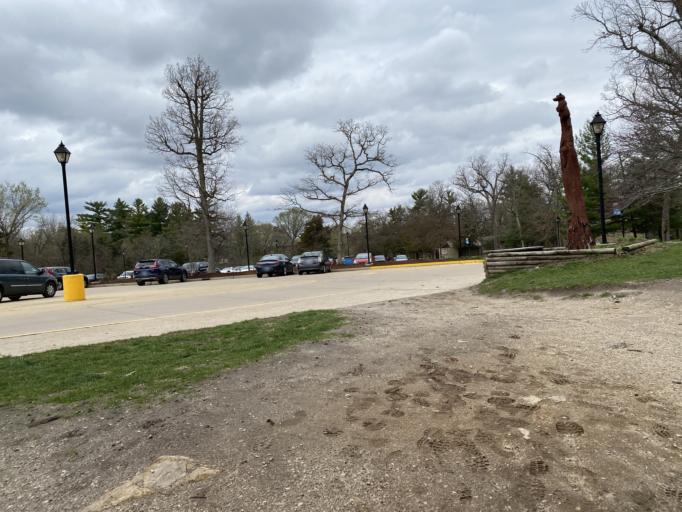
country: US
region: Illinois
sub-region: LaSalle County
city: Deer Park
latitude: 41.3177
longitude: -88.9924
